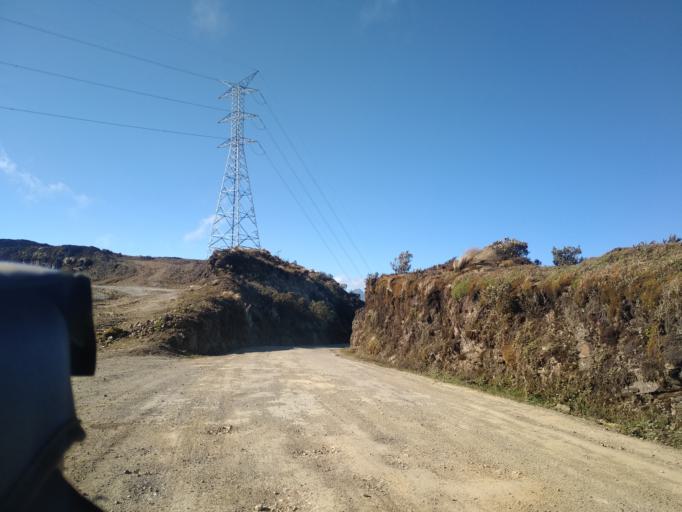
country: PE
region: Amazonas
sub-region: Provincia de Chachapoyas
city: Montevideo
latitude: -6.7334
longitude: -77.8942
